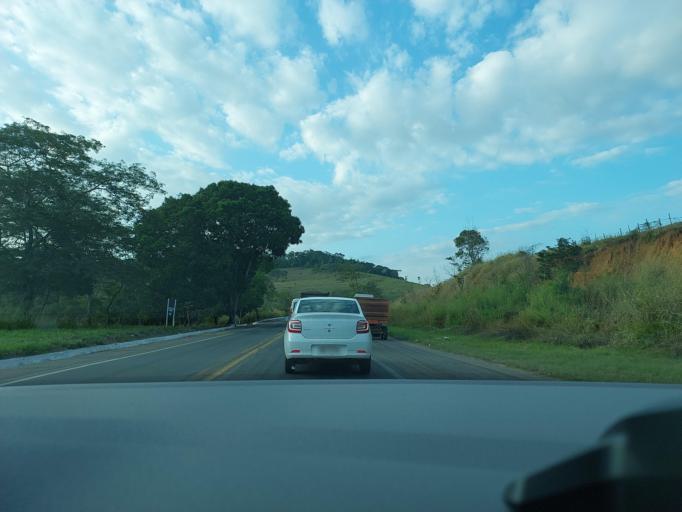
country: BR
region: Minas Gerais
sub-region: Muriae
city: Muriae
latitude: -21.1272
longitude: -42.2738
